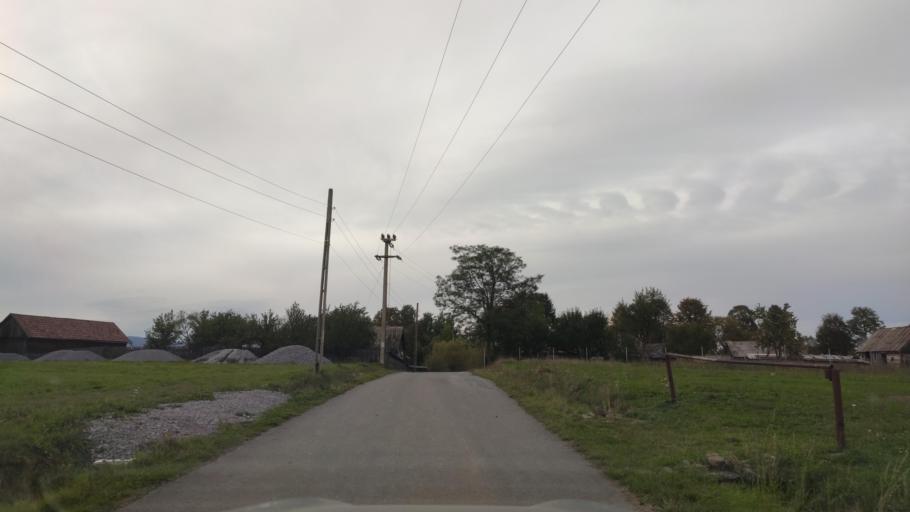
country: RO
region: Harghita
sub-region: Comuna Remetea
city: Remetea
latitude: 46.8088
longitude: 25.4375
